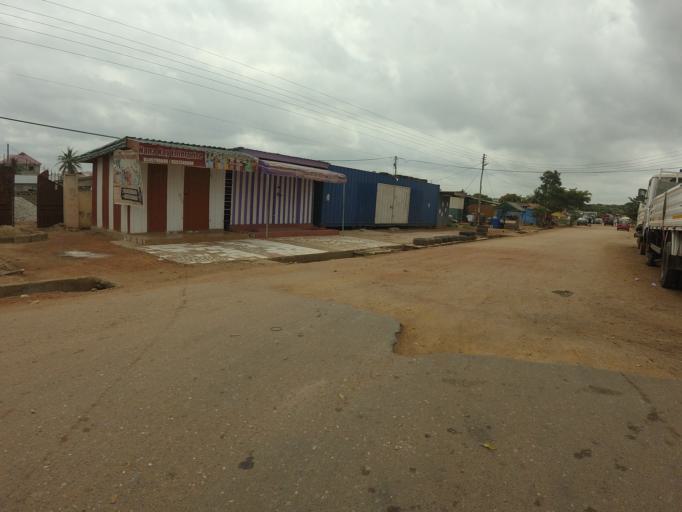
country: GH
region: Greater Accra
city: Dome
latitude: 5.6498
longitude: -0.2615
